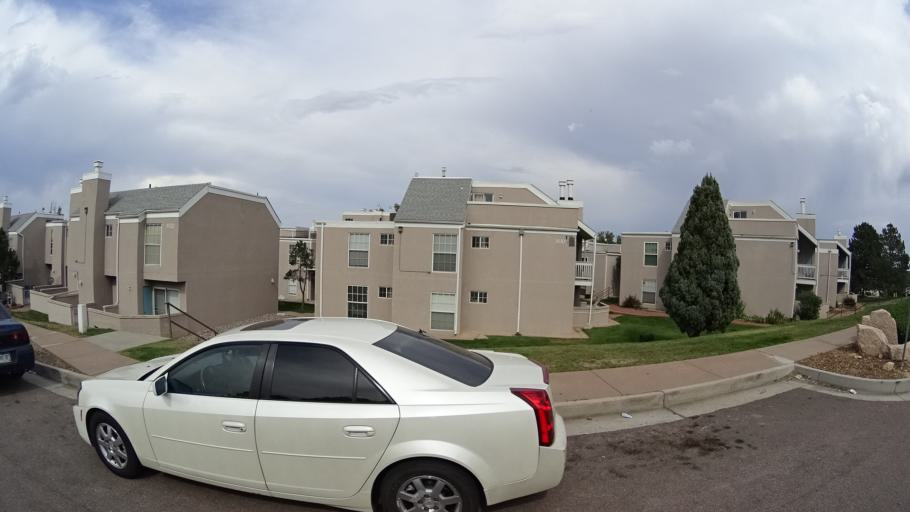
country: US
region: Colorado
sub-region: El Paso County
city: Cimarron Hills
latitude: 38.8773
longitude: -104.7626
